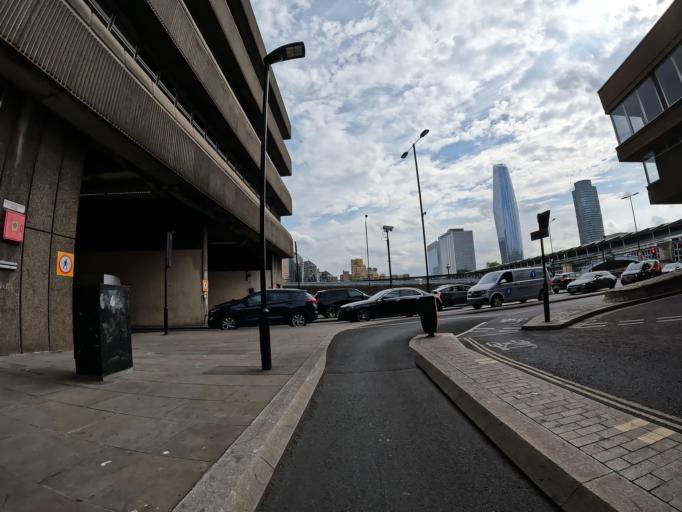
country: GB
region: England
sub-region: Greater London
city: Harringay
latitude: 51.5748
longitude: -0.0846
